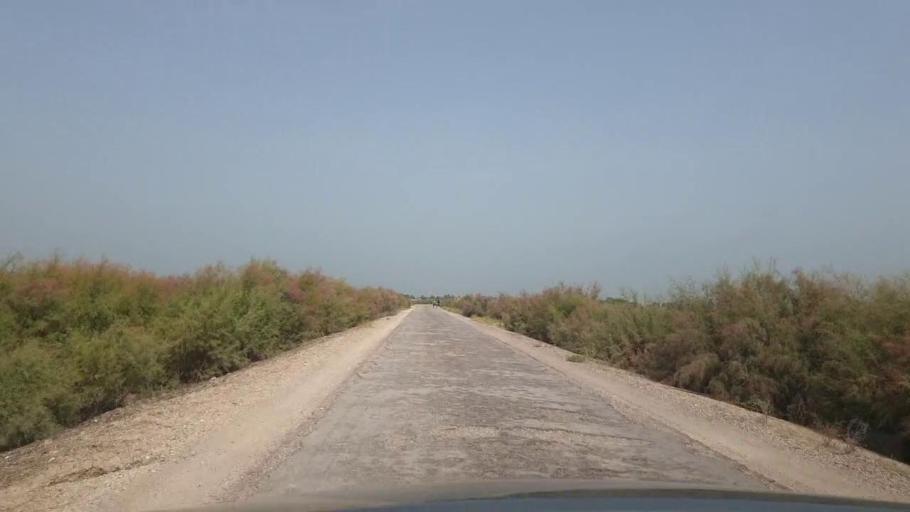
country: PK
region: Sindh
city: Madeji
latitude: 27.8347
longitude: 68.4446
